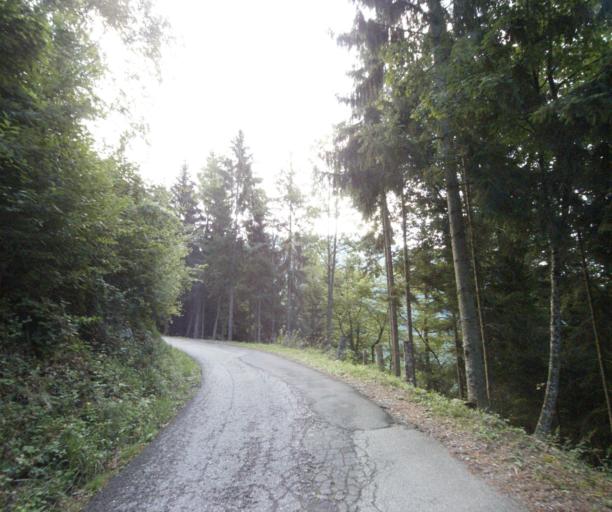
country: CH
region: Vaud
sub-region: Aigle District
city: Villeneuve
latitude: 46.4104
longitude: 6.9420
